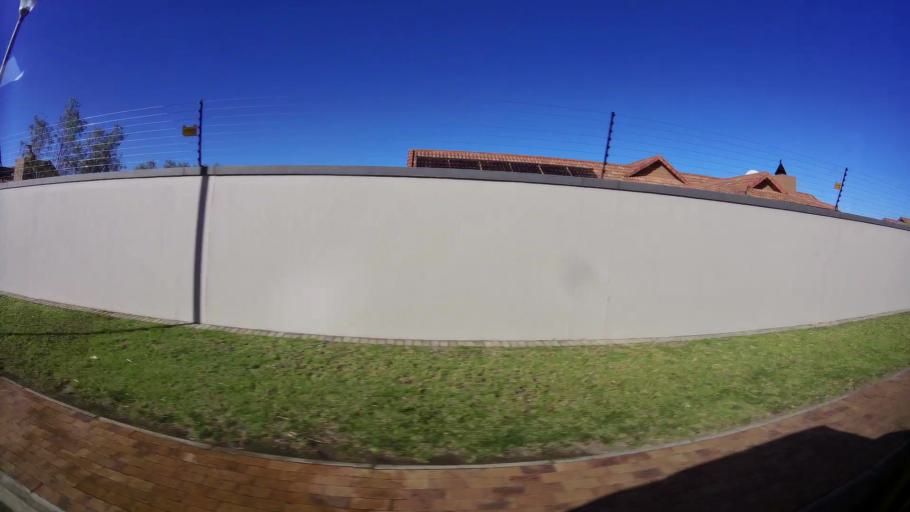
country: ZA
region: Western Cape
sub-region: Eden District Municipality
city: George
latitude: -33.9611
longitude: 22.4262
